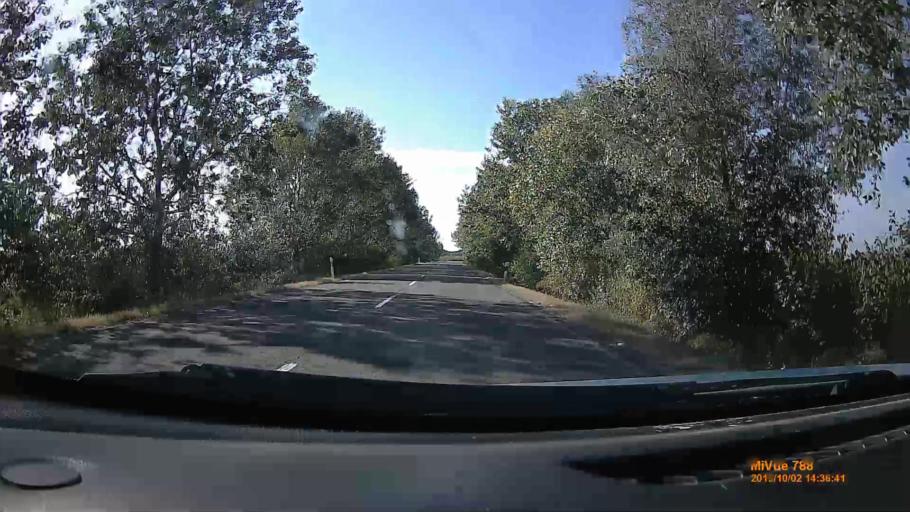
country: HU
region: Borsod-Abauj-Zemplen
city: Mezokovesd
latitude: 47.7880
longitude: 20.5658
